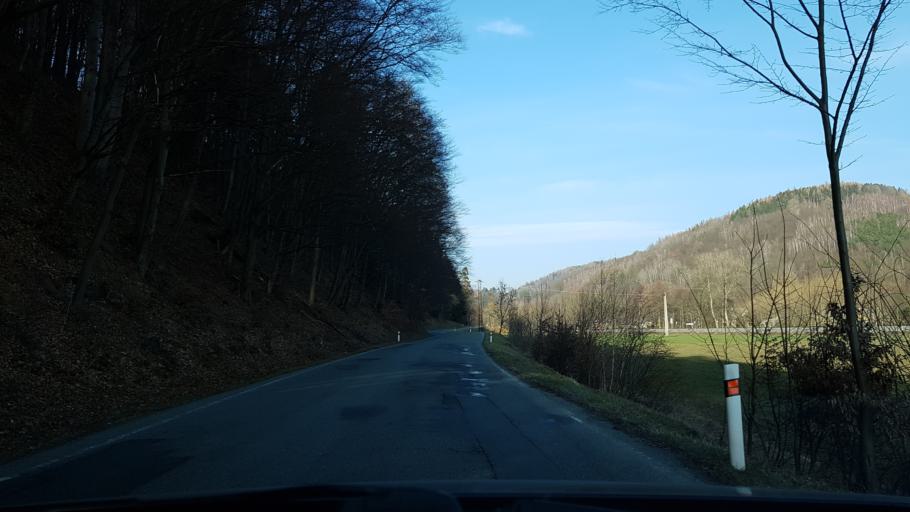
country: CZ
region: Olomoucky
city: Dolni Bohdikov
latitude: 50.0134
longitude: 16.8963
